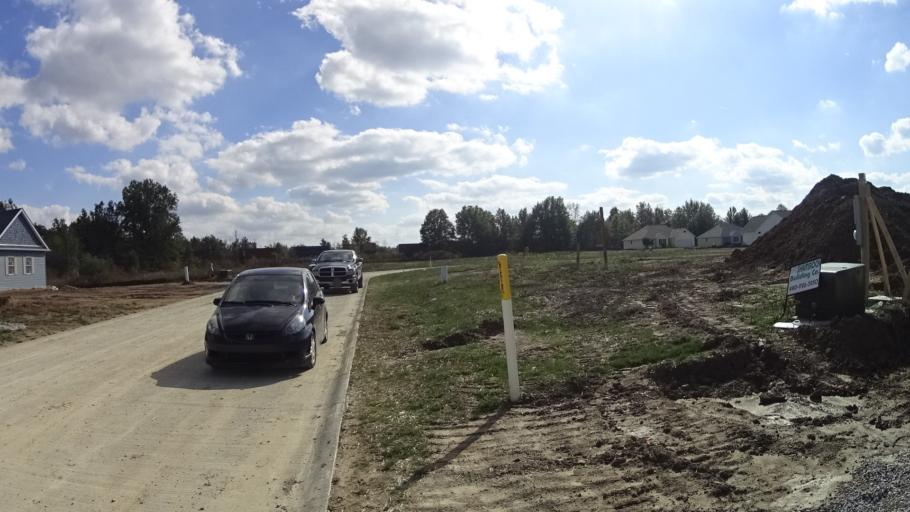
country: US
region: Ohio
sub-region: Lorain County
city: Grafton
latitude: 41.2827
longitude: -82.0460
